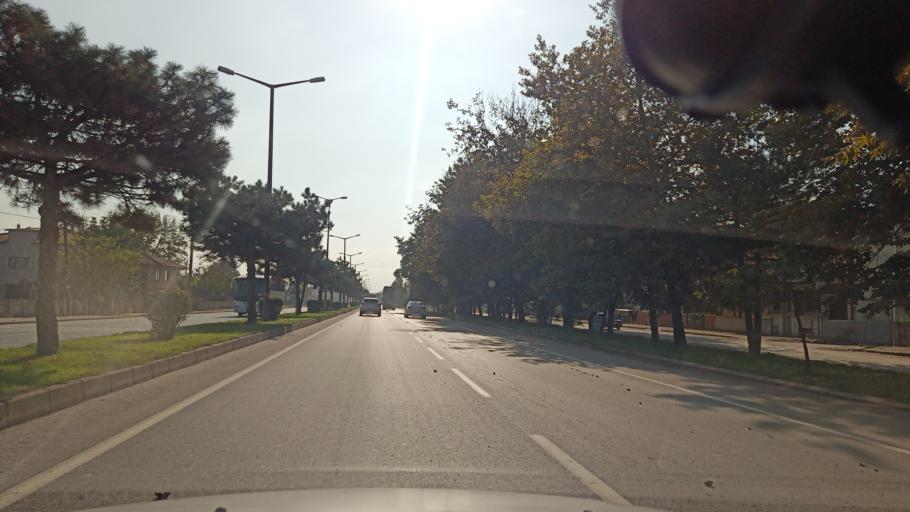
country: TR
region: Sakarya
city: Adapazari
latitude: 40.8080
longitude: 30.4055
